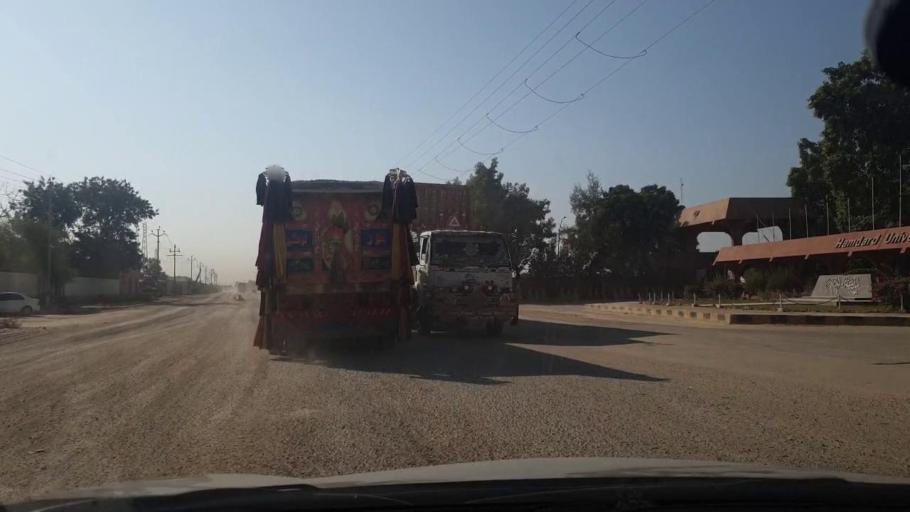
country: PK
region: Sindh
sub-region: Karachi District
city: Karachi
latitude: 25.0838
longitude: 67.0126
